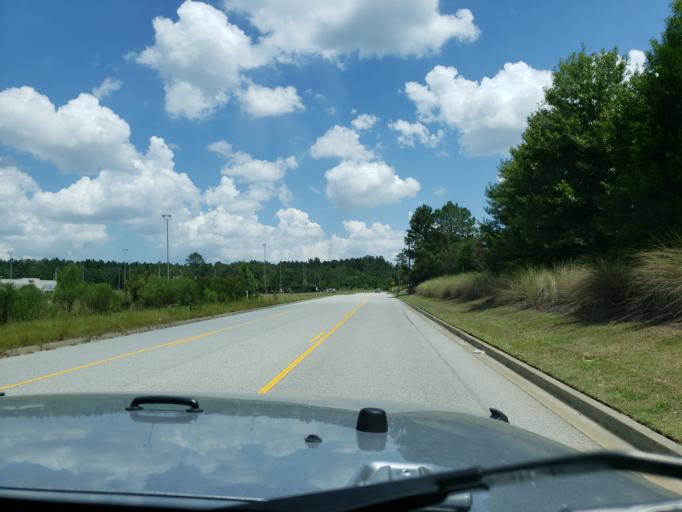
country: US
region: Georgia
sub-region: Chatham County
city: Bloomingdale
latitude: 32.1126
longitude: -81.2854
